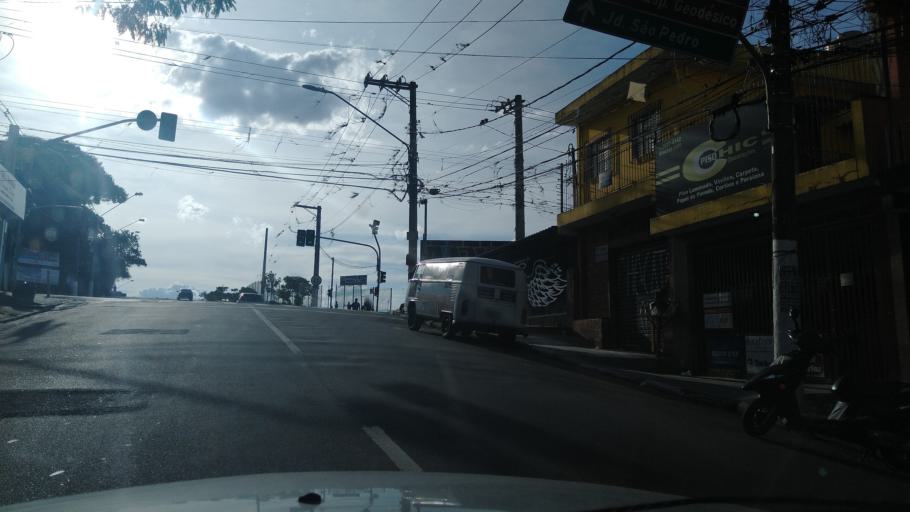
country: BR
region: Sao Paulo
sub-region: Osasco
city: Osasco
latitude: -23.5323
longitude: -46.8060
